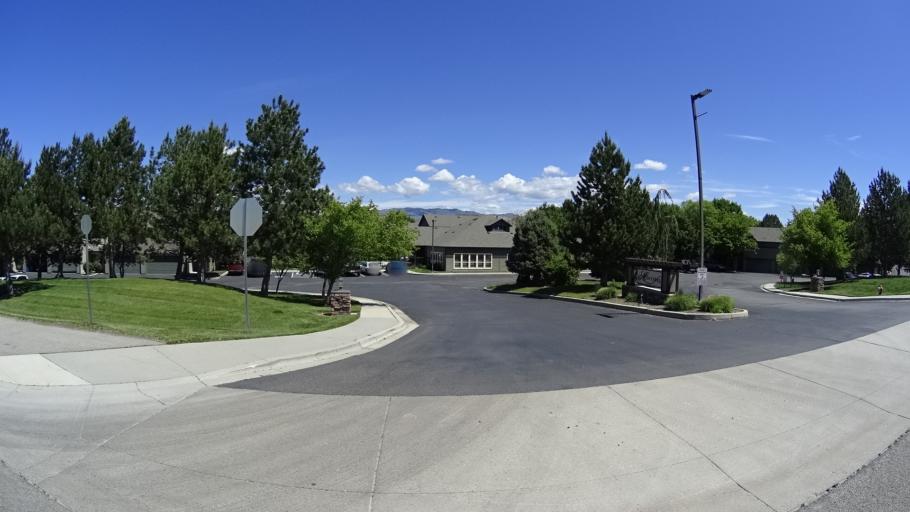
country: US
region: Idaho
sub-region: Ada County
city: Boise
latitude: 43.5655
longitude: -116.1782
